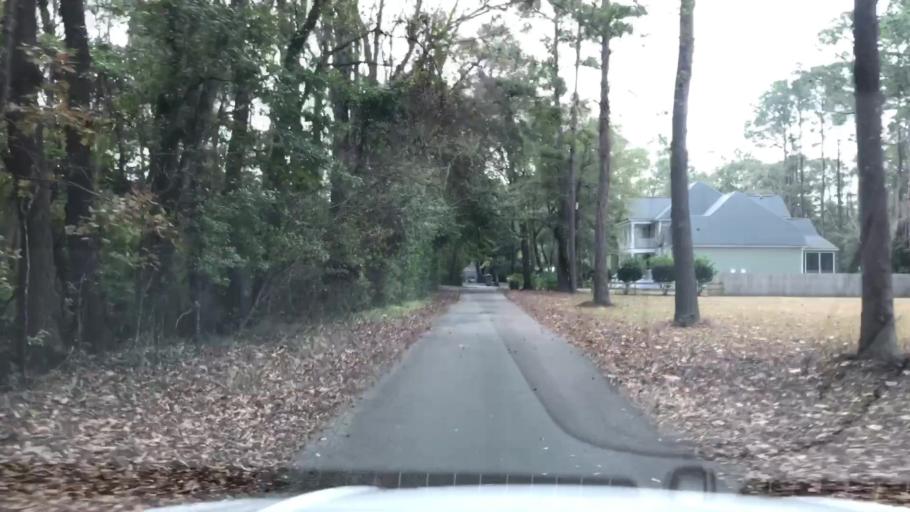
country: US
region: South Carolina
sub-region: Charleston County
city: Kiawah Island
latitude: 32.6798
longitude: -80.0354
